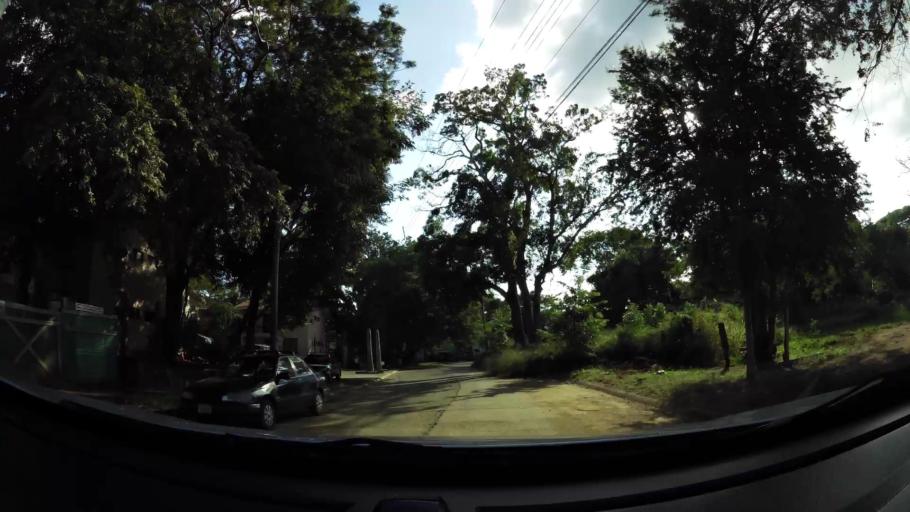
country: CR
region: Guanacaste
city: Sardinal
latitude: 10.5556
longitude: -85.6914
